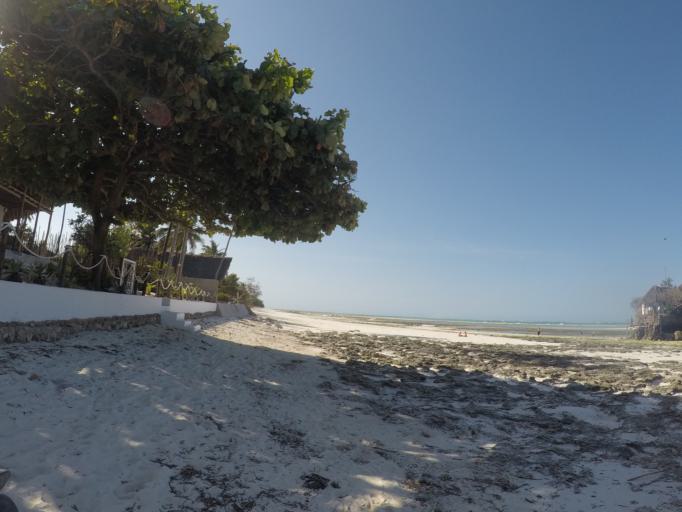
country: TZ
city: Kiwengwa
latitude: -6.1527
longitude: 39.5188
